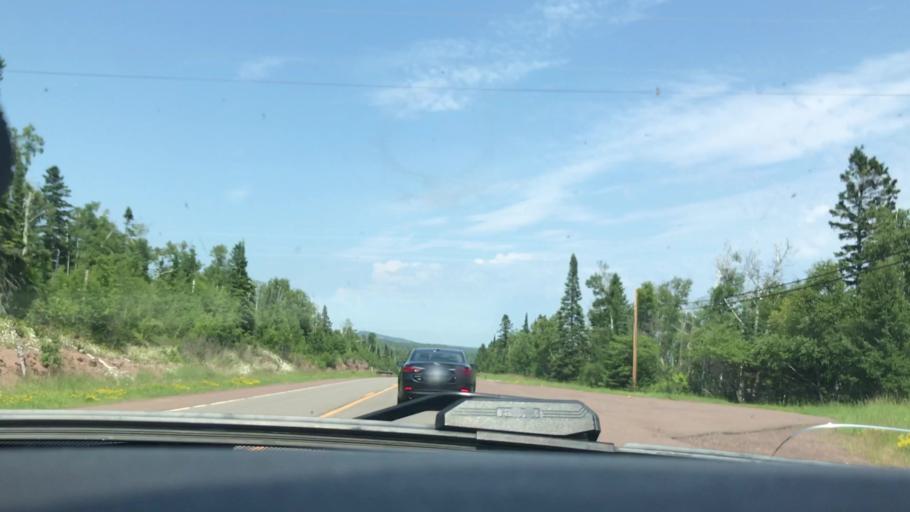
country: US
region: Minnesota
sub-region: Cook County
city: Grand Marais
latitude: 47.5964
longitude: -90.7935
